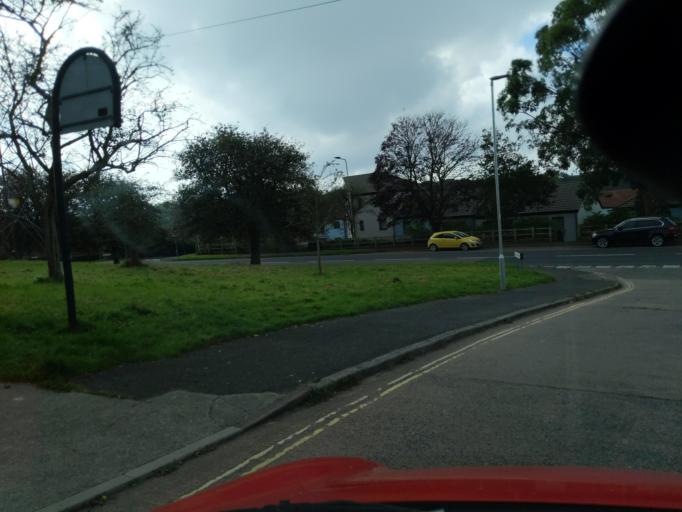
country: GB
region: England
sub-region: Plymouth
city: Plymouth
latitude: 50.4190
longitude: -4.1565
